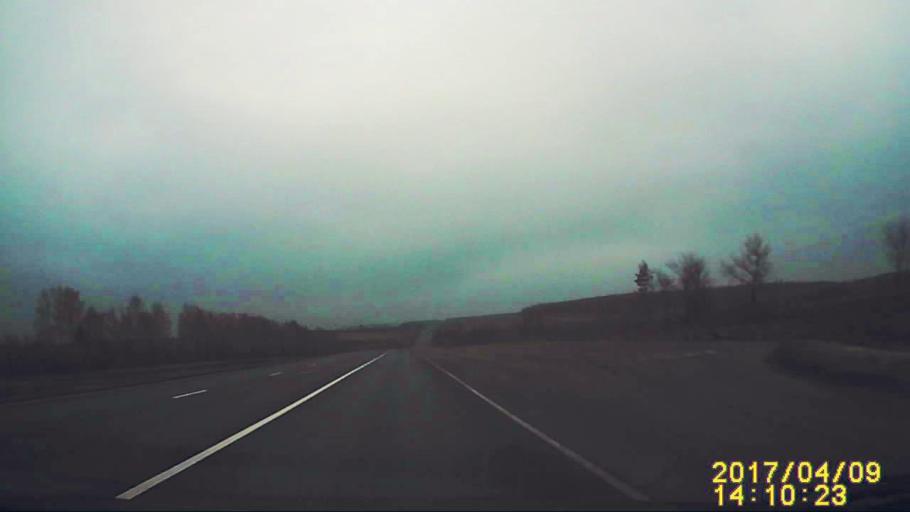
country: RU
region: Ulyanovsk
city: Krasnyy Gulyay
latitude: 54.0378
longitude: 48.2133
